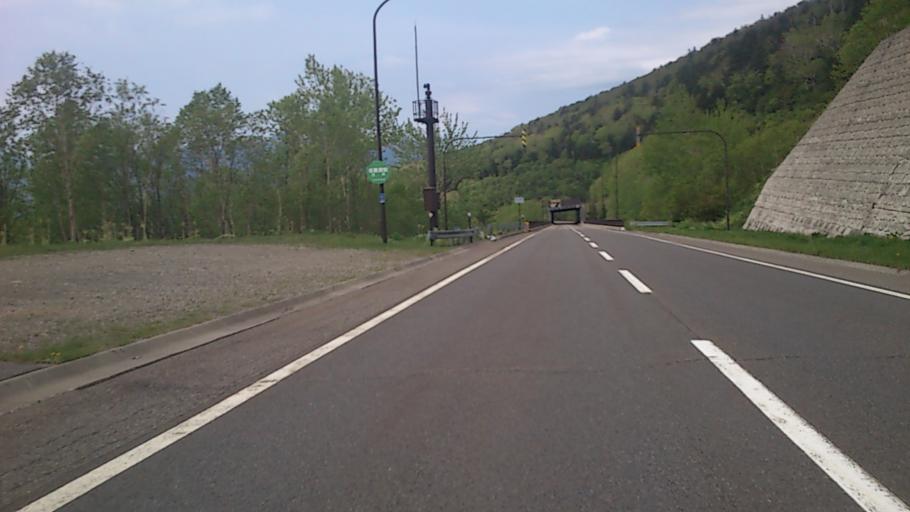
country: JP
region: Hokkaido
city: Kamikawa
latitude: 43.5718
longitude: 143.1215
